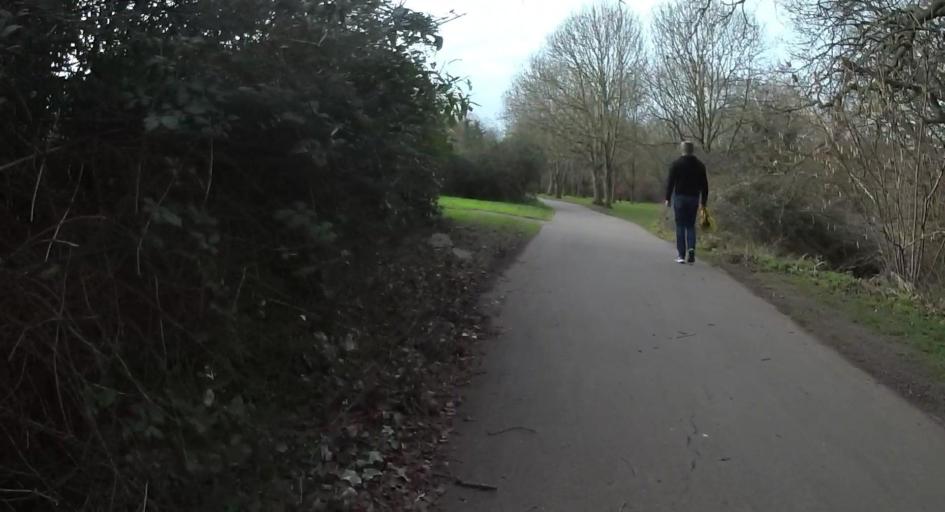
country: GB
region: England
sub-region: Wokingham
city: Wokingham
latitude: 51.4107
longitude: -0.8506
